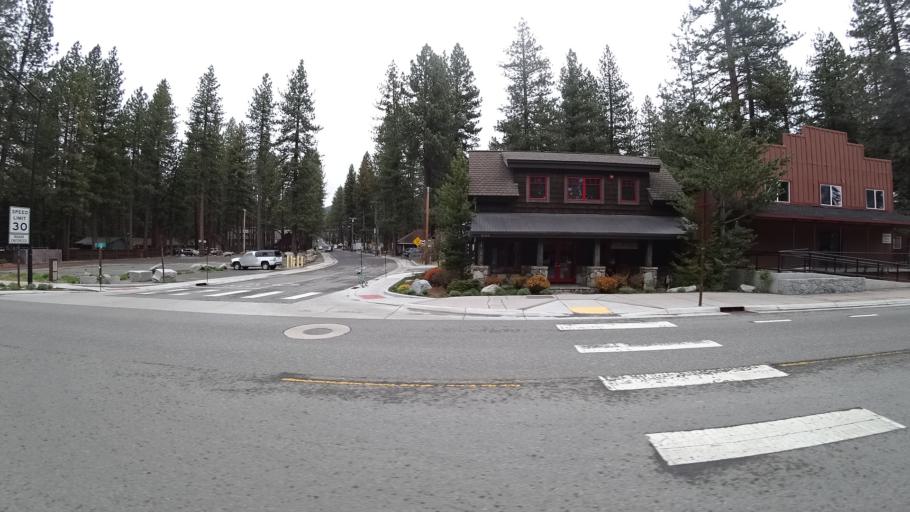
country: US
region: California
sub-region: Placer County
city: Kings Beach
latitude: 39.2351
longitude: -120.0195
